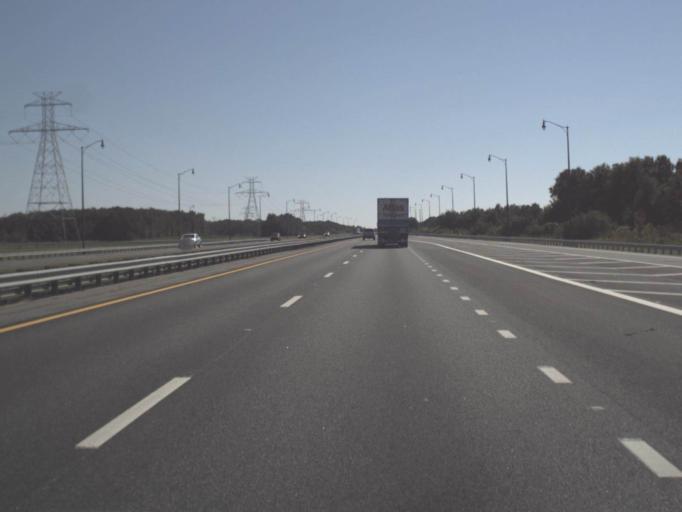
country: US
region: Florida
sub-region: Lake County
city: Hawthorne
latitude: 28.7540
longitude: -81.9375
